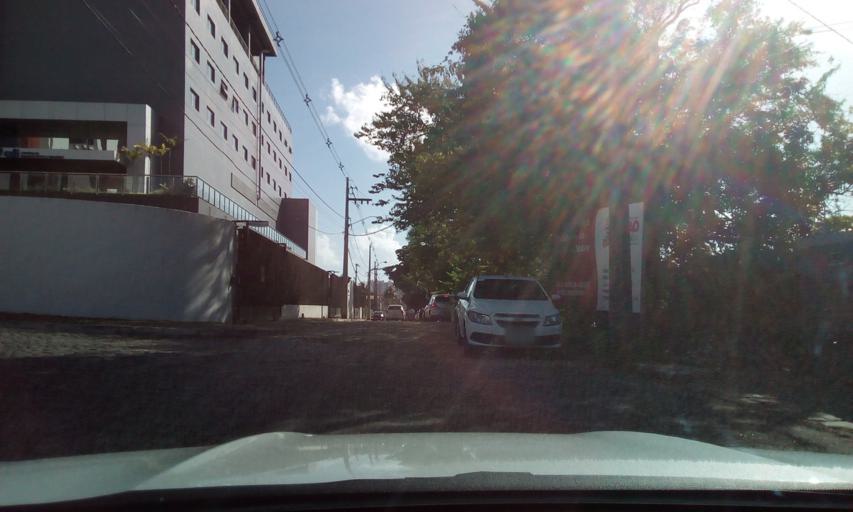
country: BR
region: Paraiba
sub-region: Joao Pessoa
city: Joao Pessoa
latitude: -7.1337
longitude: -34.8590
